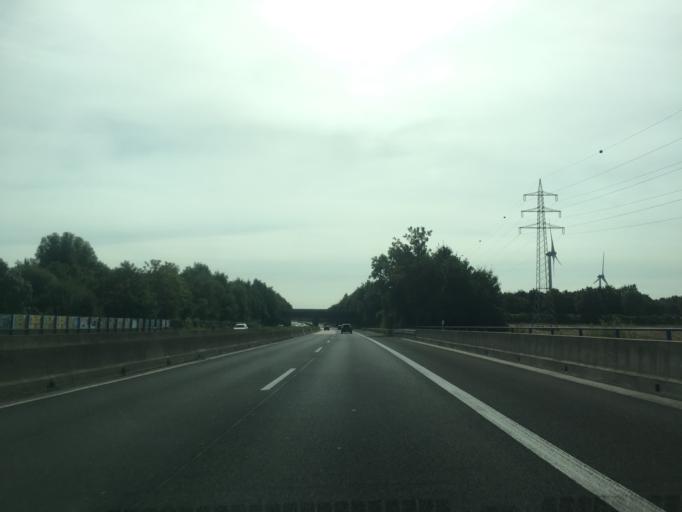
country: DE
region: North Rhine-Westphalia
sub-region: Regierungsbezirk Koln
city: Bedburg
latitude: 50.9697
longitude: 6.5635
